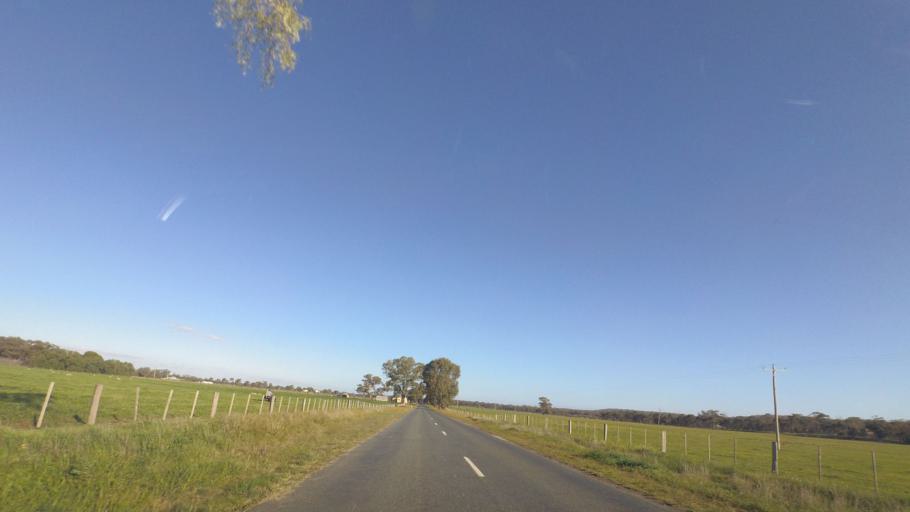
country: AU
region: Victoria
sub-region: Greater Bendigo
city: Epsom
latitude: -36.7195
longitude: 144.5132
